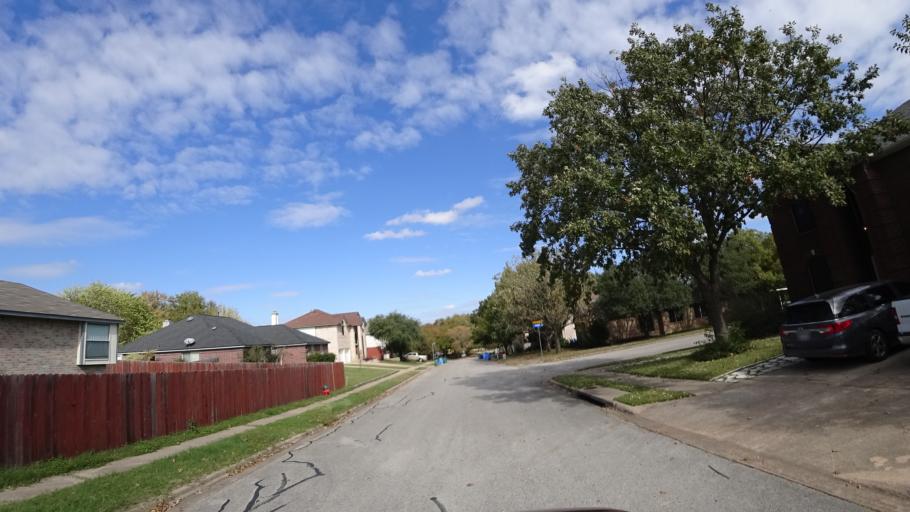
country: US
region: Texas
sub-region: Travis County
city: Pflugerville
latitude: 30.4446
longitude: -97.6228
